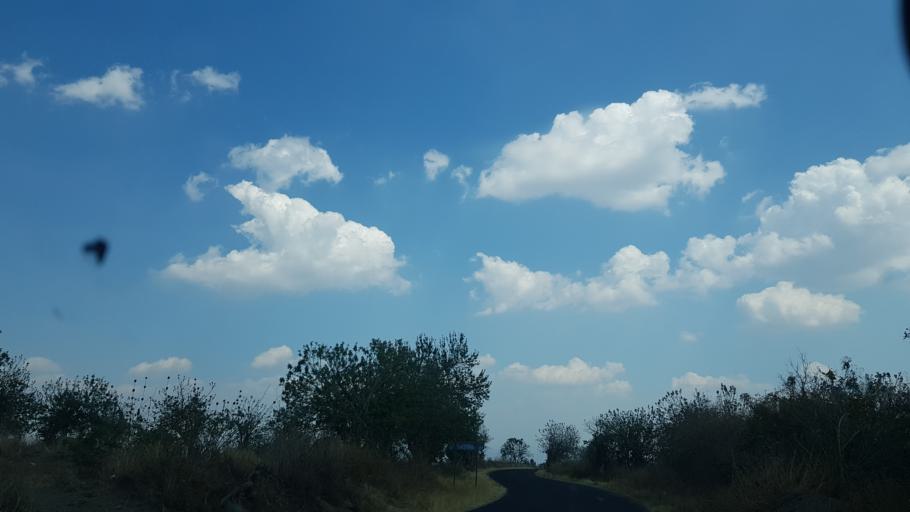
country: MX
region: Puebla
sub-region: Atlixco
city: San Pedro Benito Juarez
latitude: 18.9487
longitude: -98.5399
